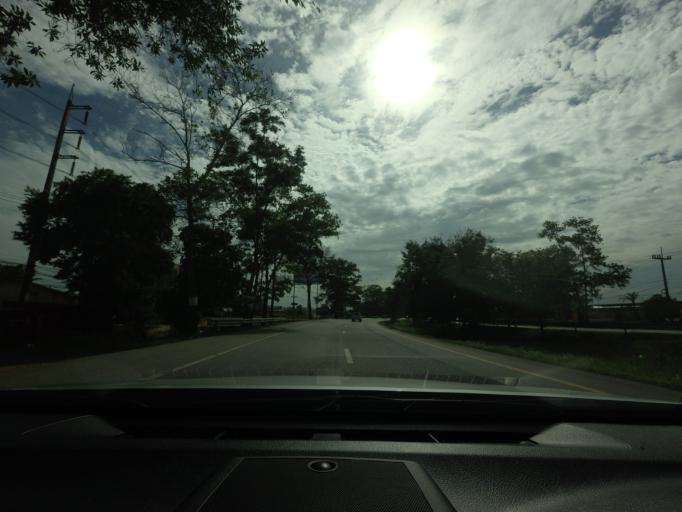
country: TH
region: Songkhla
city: Hat Yai
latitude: 6.9876
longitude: 100.4218
